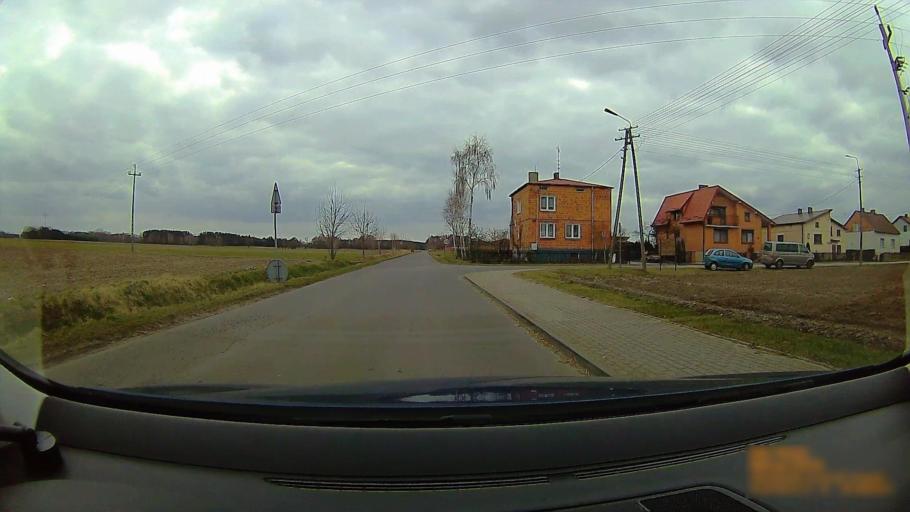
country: PL
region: Greater Poland Voivodeship
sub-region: Powiat koninski
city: Rychwal
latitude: 52.0920
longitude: 18.1404
